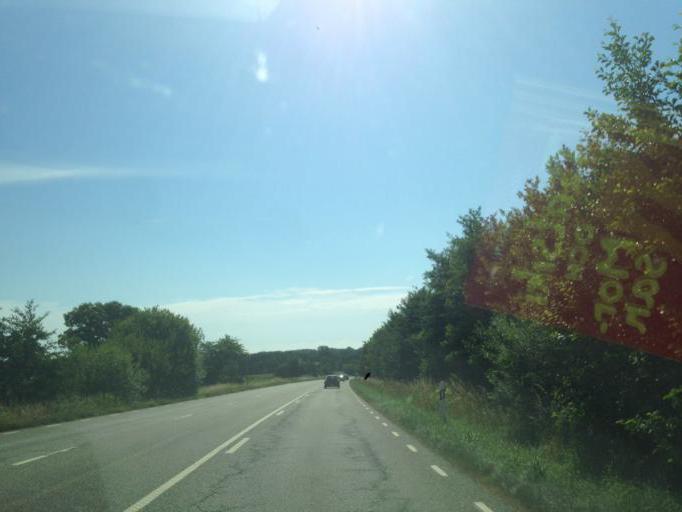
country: SE
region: Skane
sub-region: Simrishamns Kommun
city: Kivik
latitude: 55.6357
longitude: 14.2415
